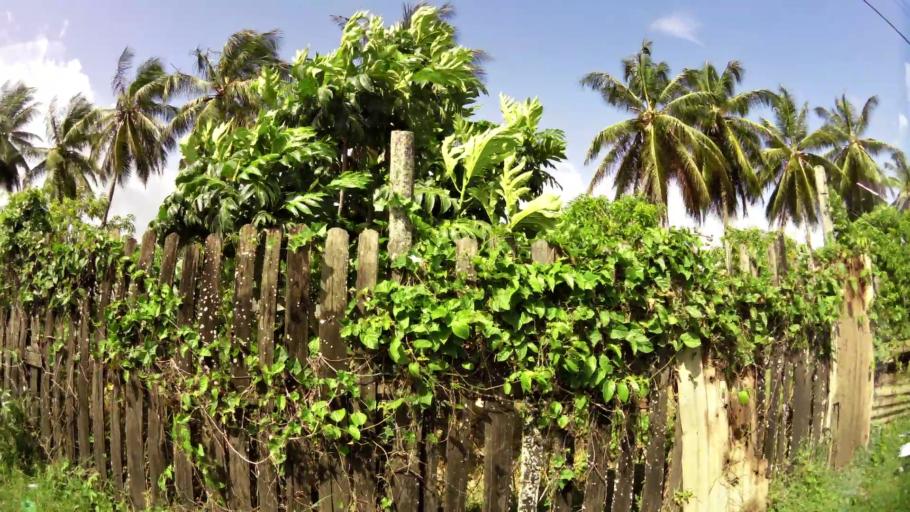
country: GY
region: Demerara-Mahaica
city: Mahaica Village
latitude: 6.7620
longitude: -57.9923
